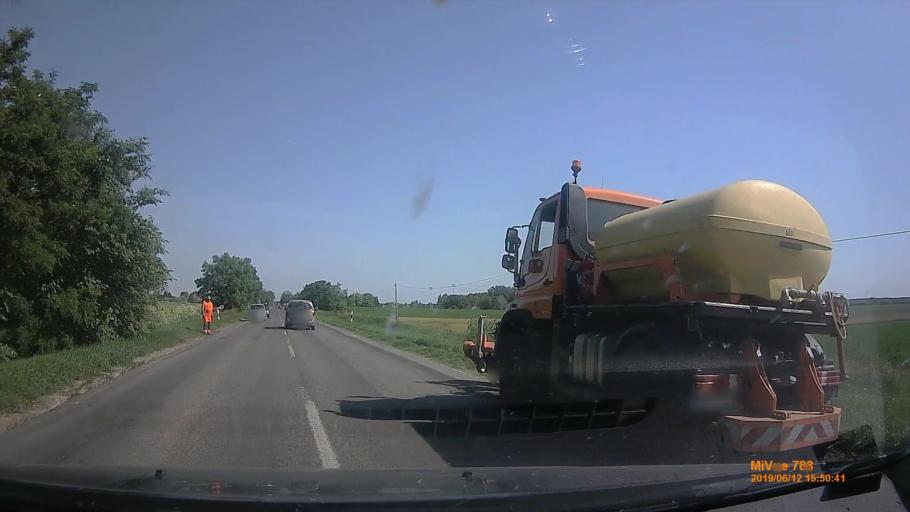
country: HU
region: Csongrad
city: Apatfalva
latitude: 46.1858
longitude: 20.5667
